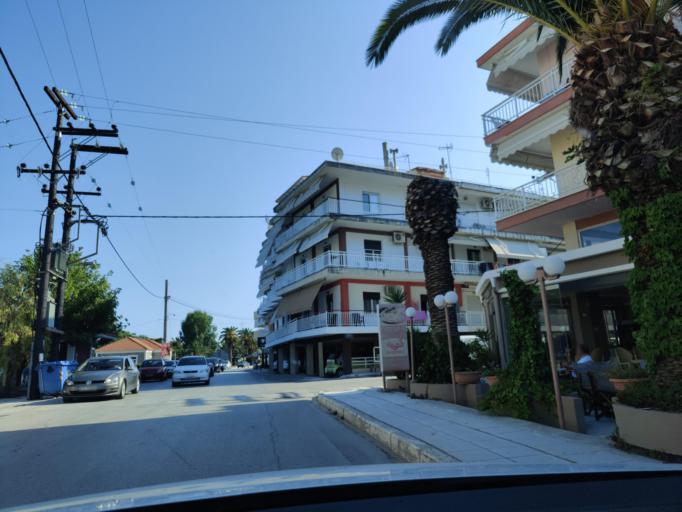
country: GR
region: East Macedonia and Thrace
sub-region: Nomos Kavalas
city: Nea Peramos
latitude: 40.8424
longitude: 24.3055
